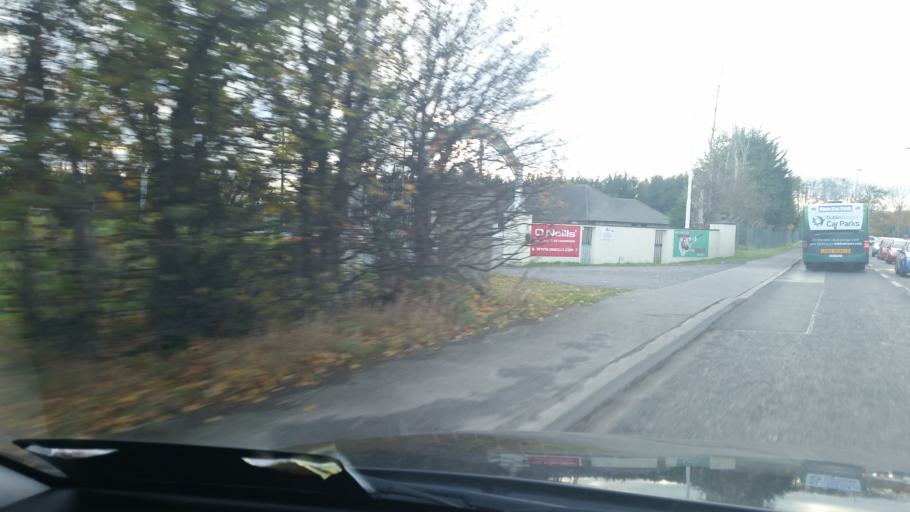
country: IE
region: Leinster
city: Ballymun
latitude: 53.4178
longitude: -6.2641
